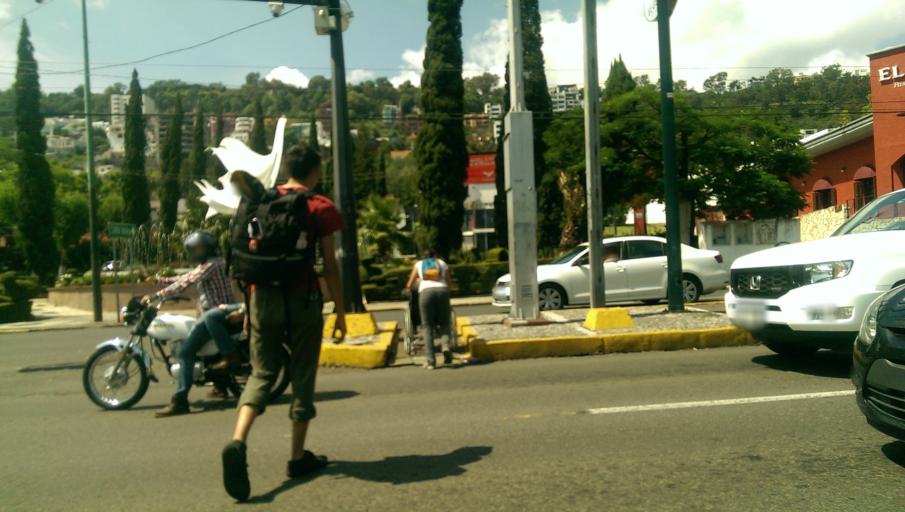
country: MX
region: Michoacan
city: Morelia
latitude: 19.6814
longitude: -101.1815
